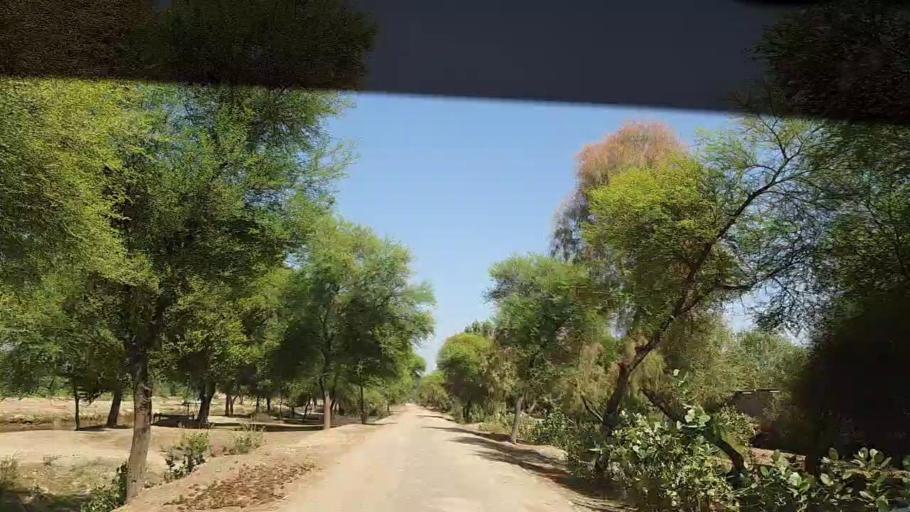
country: PK
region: Sindh
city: Tangwani
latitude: 28.2905
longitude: 69.0721
